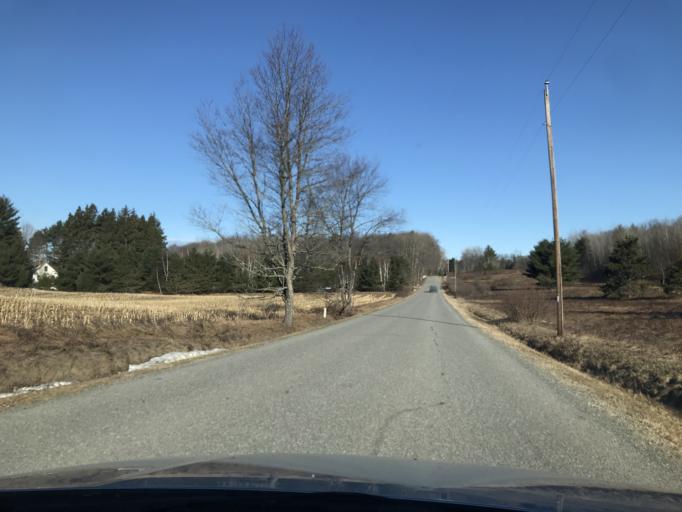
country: US
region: Wisconsin
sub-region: Marinette County
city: Niagara
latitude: 45.3851
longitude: -88.0423
